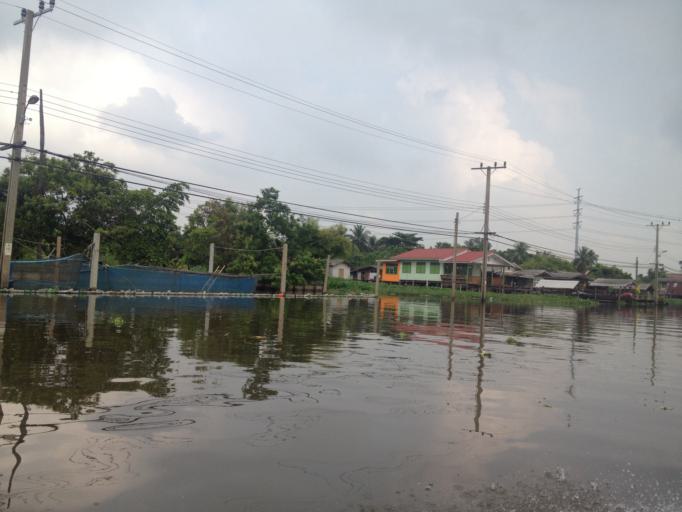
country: TH
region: Nonthaburi
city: Bang Kruai
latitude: 13.7970
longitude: 100.4705
